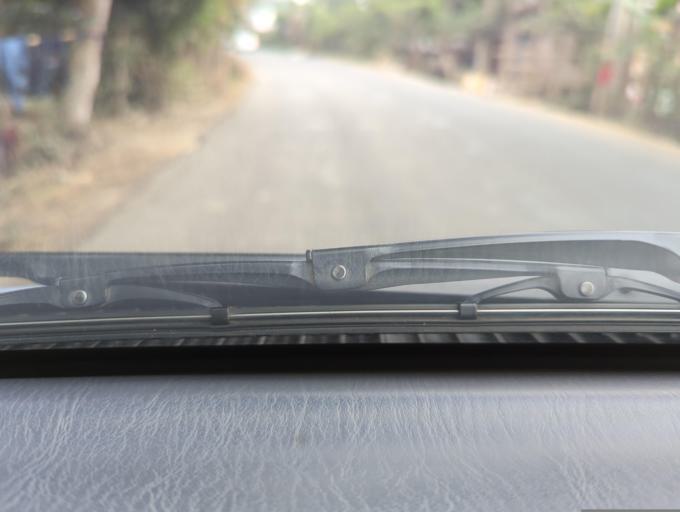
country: BD
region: Sylhet
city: Maulavi Bazar
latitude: 24.5097
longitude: 91.7265
